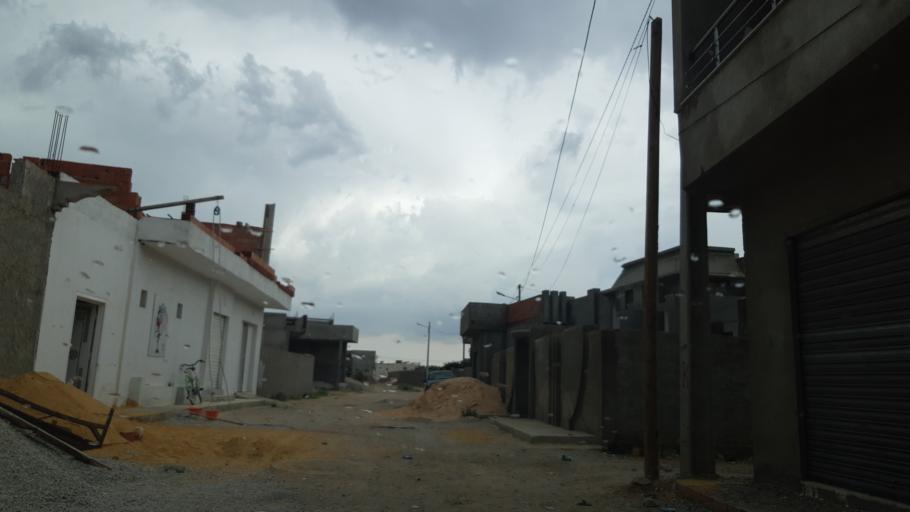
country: TN
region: Al Qayrawan
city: Sbikha
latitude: 36.1230
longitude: 10.0901
